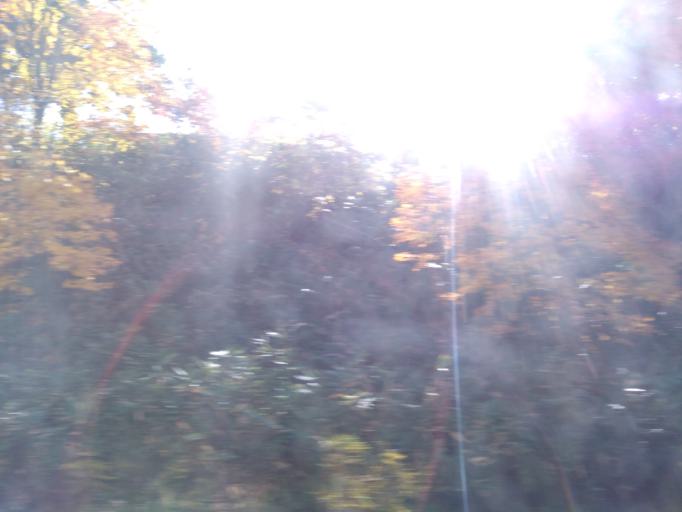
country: JP
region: Hokkaido
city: Kitahiroshima
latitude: 42.9944
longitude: 141.5475
